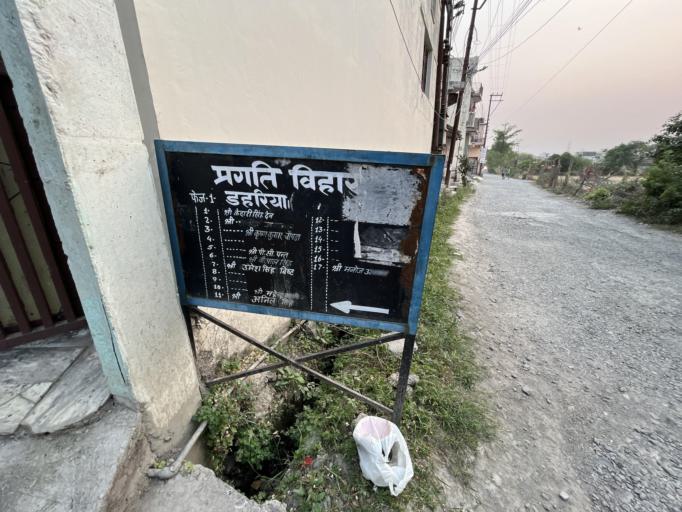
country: IN
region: Uttarakhand
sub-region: Naini Tal
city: Haldwani
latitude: 29.2046
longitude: 79.5131
